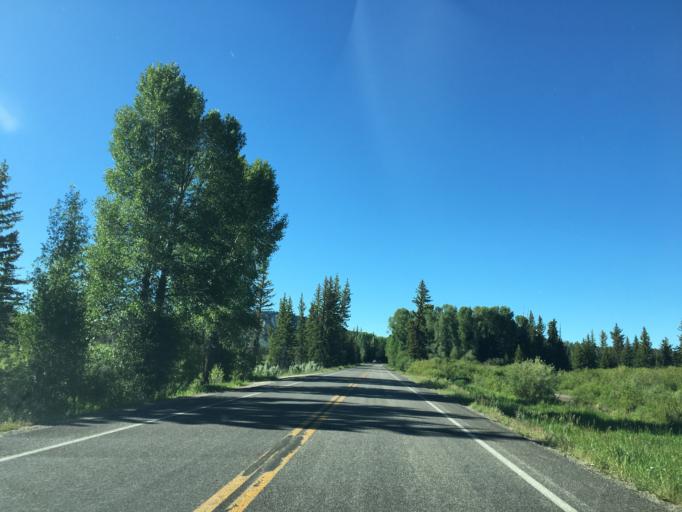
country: US
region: Wyoming
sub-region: Teton County
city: Jackson
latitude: 43.8331
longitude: -110.5133
